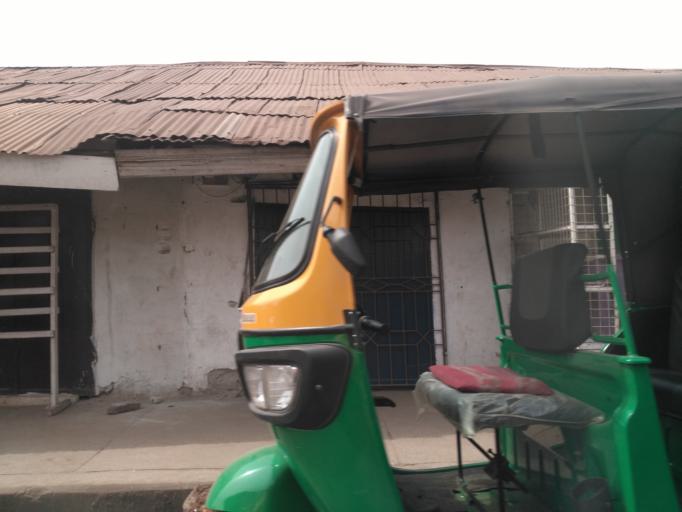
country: GH
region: Ashanti
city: Kumasi
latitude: 6.6984
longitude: -1.5965
